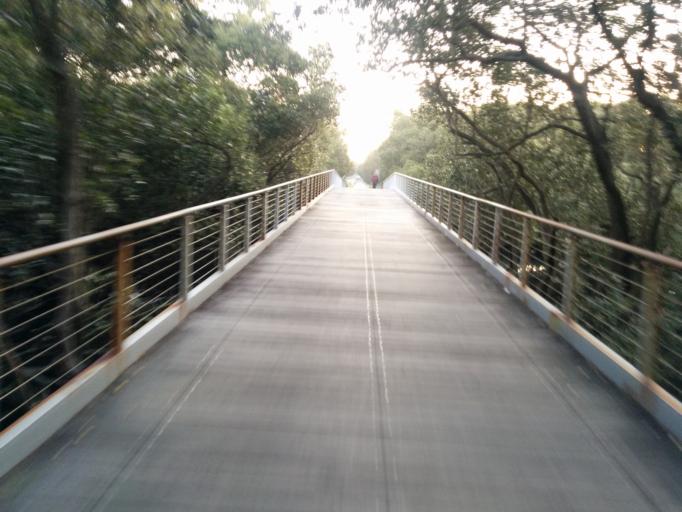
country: AU
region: New South Wales
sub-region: Canada Bay
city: Concord West
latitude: -33.8448
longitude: 151.0806
